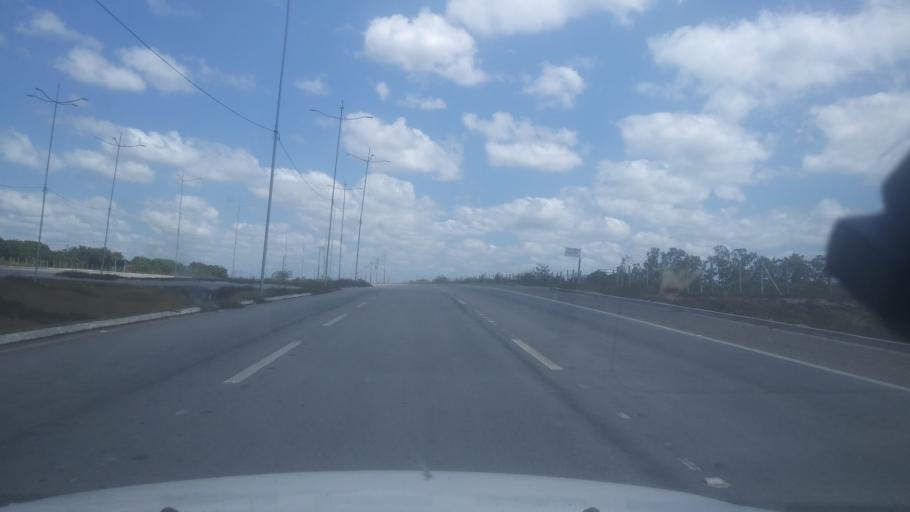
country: BR
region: Rio Grande do Norte
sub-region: Macaiba
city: Macaiba
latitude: -5.8471
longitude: -35.3781
